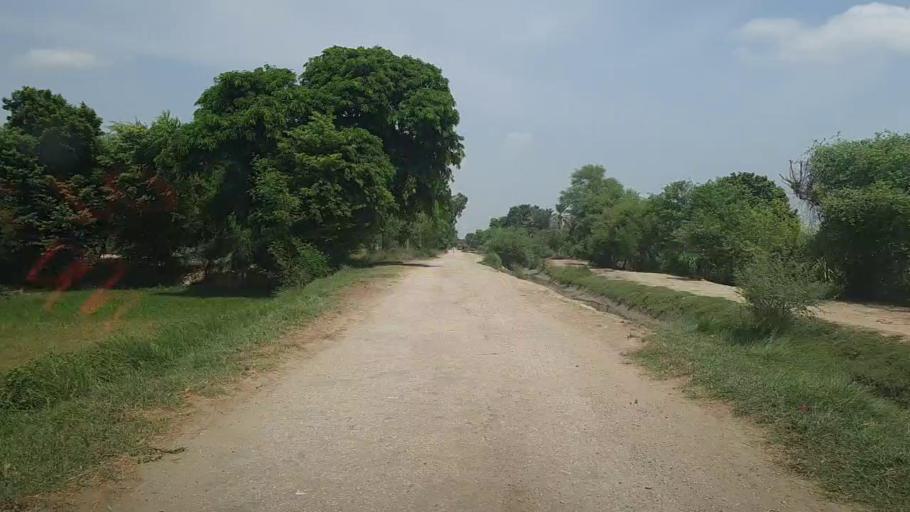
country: PK
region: Sindh
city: Ubauro
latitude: 28.2906
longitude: 69.7999
